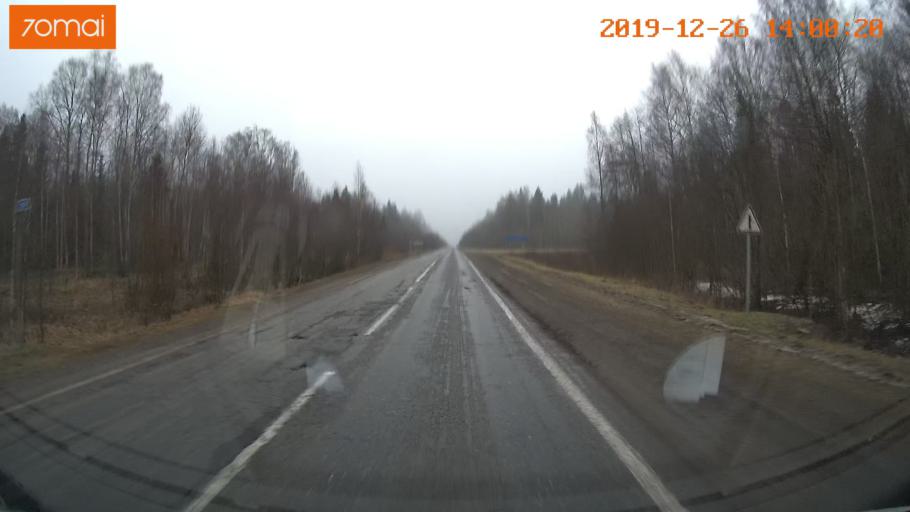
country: RU
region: Jaroslavl
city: Poshekhon'ye
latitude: 58.5589
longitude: 38.7414
